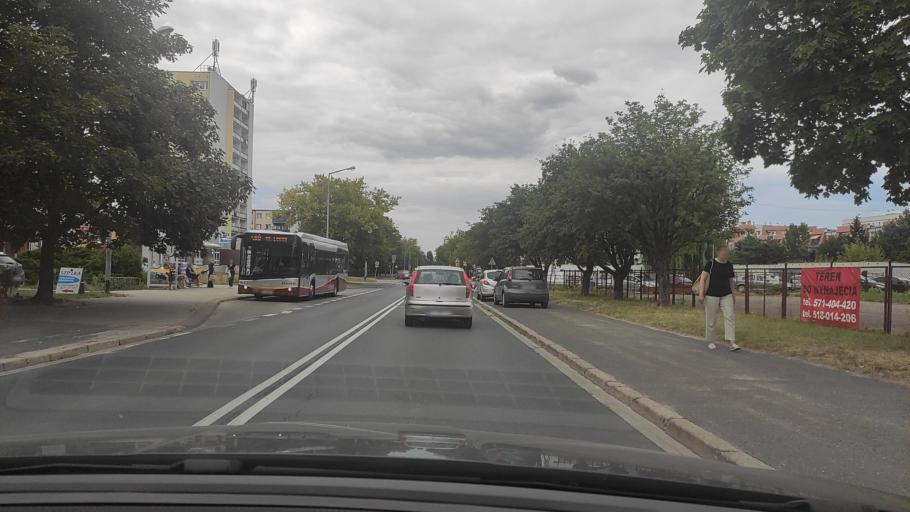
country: PL
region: Greater Poland Voivodeship
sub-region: Powiat poznanski
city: Swarzedz
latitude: 52.4163
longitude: 17.0833
